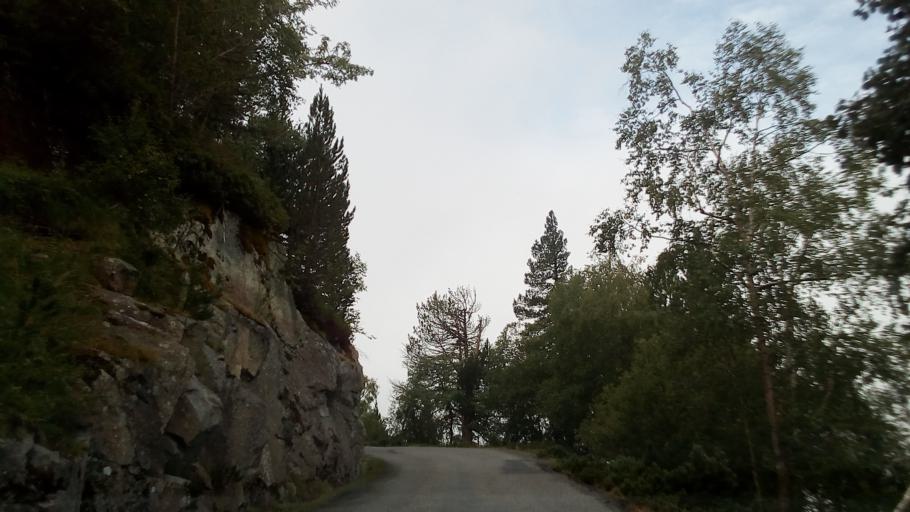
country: FR
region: Midi-Pyrenees
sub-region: Departement des Hautes-Pyrenees
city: Saint-Lary-Soulan
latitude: 42.8233
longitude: 0.1636
